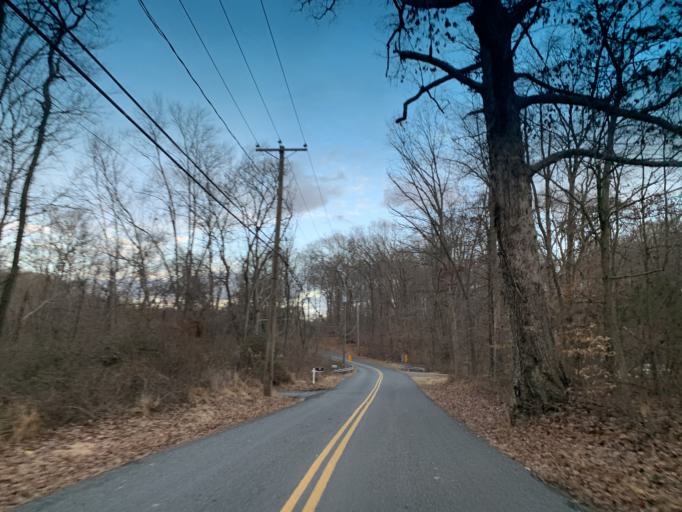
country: US
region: Pennsylvania
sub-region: York County
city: Susquehanna Trails
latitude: 39.6563
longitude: -76.3019
